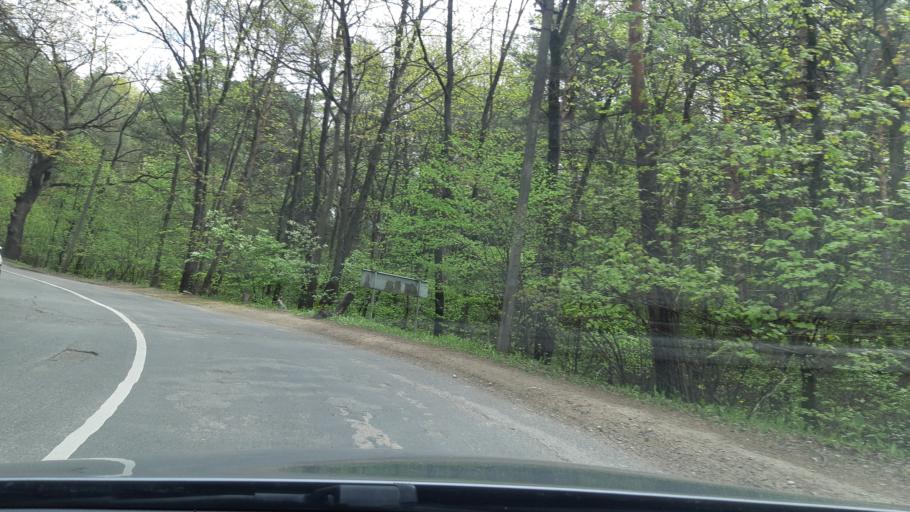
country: LT
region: Kauno apskritis
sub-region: Kauno rajonas
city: Akademija (Kaunas)
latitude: 54.9231
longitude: 23.8277
